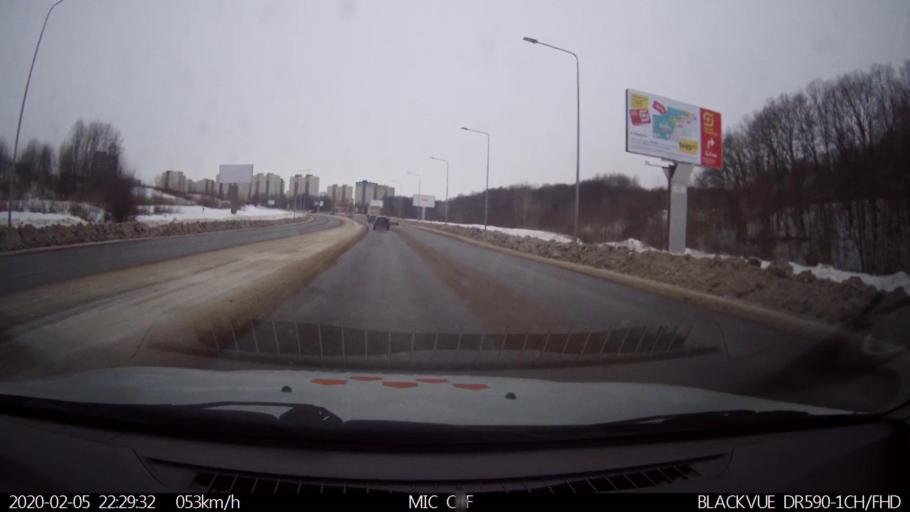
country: RU
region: Nizjnij Novgorod
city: Imeni Stepana Razina
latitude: 54.7487
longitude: 44.1457
